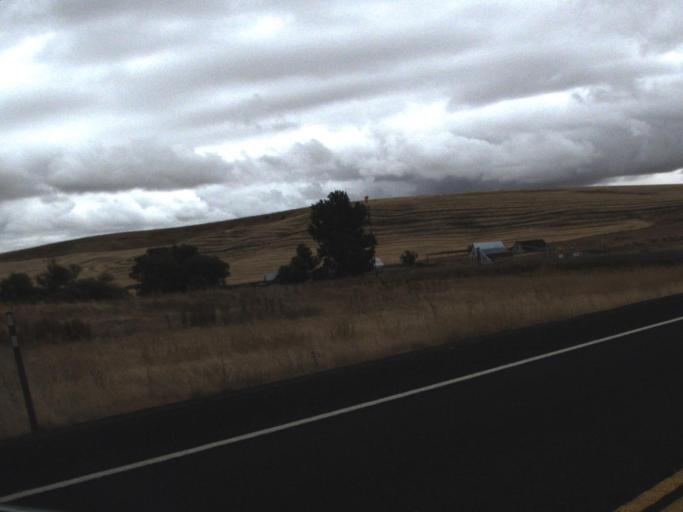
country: US
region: Washington
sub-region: Whitman County
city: Colfax
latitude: 47.2090
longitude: -117.3578
